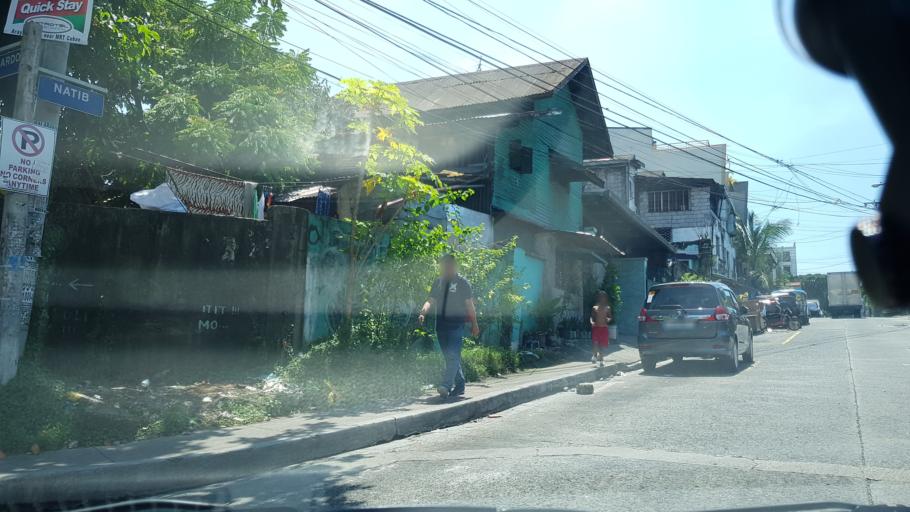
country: PH
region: Metro Manila
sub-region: San Juan
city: San Juan
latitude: 14.6198
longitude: 121.0476
